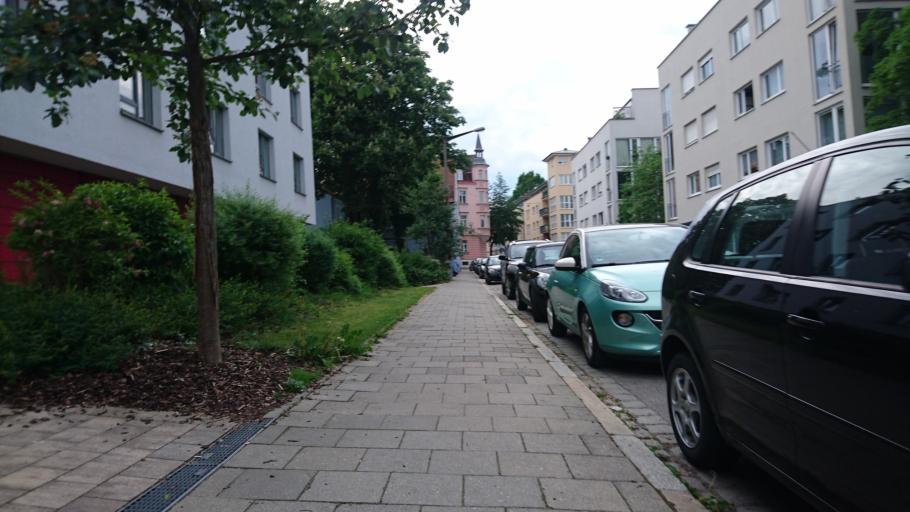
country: DE
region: Bavaria
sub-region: Upper Palatinate
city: Regensburg
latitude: 49.0124
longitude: 12.1065
